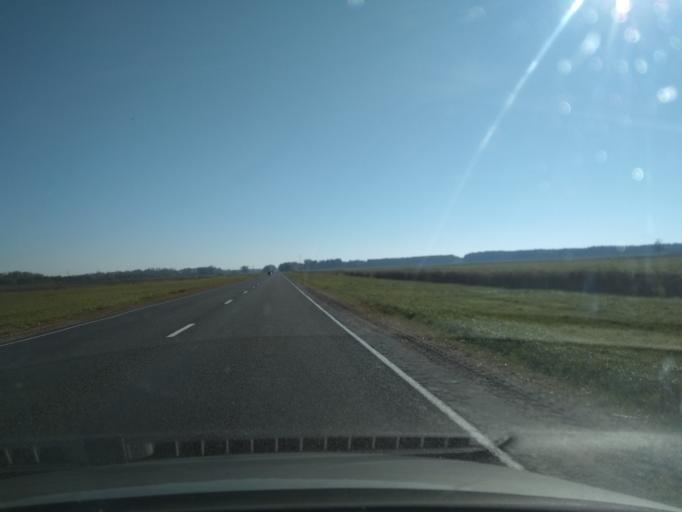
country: BY
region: Brest
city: Malaryta
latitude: 51.9420
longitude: 24.0309
